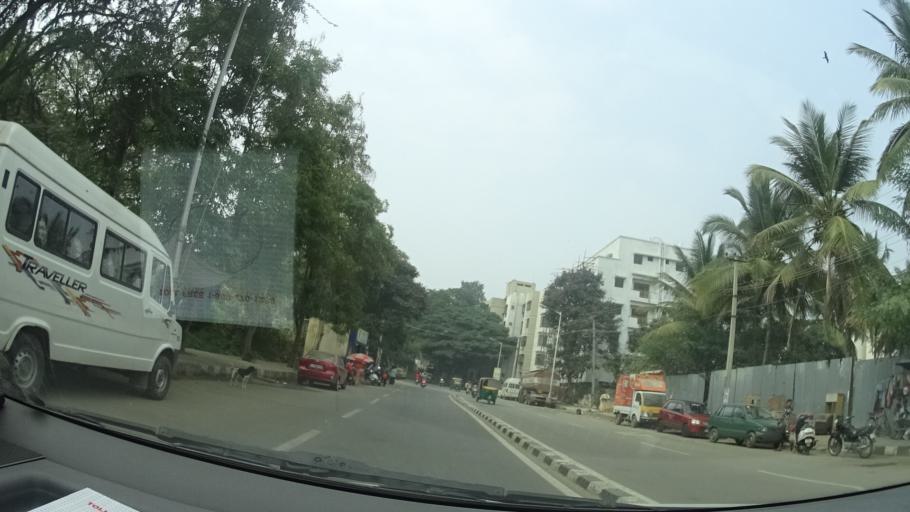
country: IN
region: Karnataka
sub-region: Bangalore Urban
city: Bangalore
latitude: 13.0212
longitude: 77.6253
